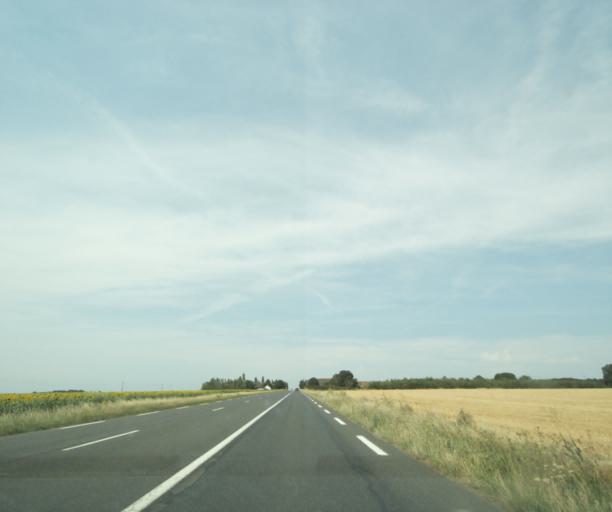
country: FR
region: Centre
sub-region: Departement d'Indre-et-Loire
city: Sainte-Maure-de-Touraine
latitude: 47.1691
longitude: 0.6529
